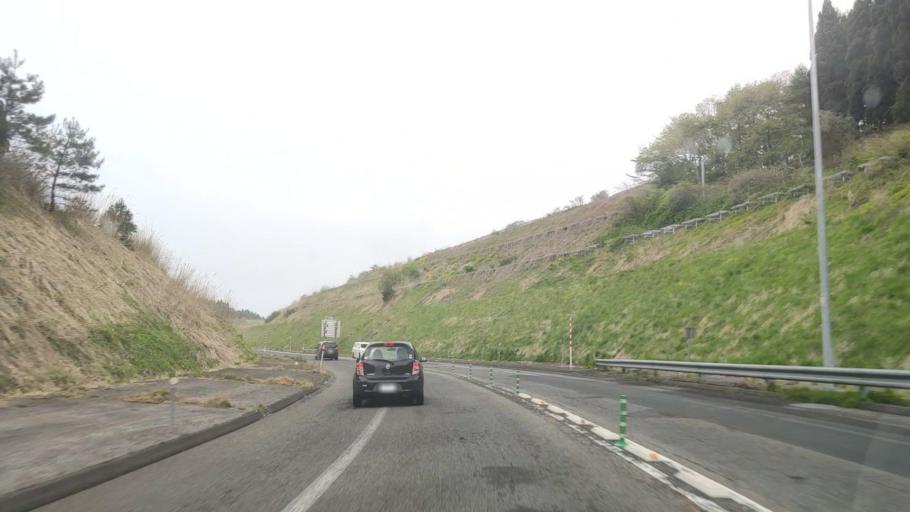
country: JP
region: Akita
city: Noshiromachi
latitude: 40.2109
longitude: 140.1944
